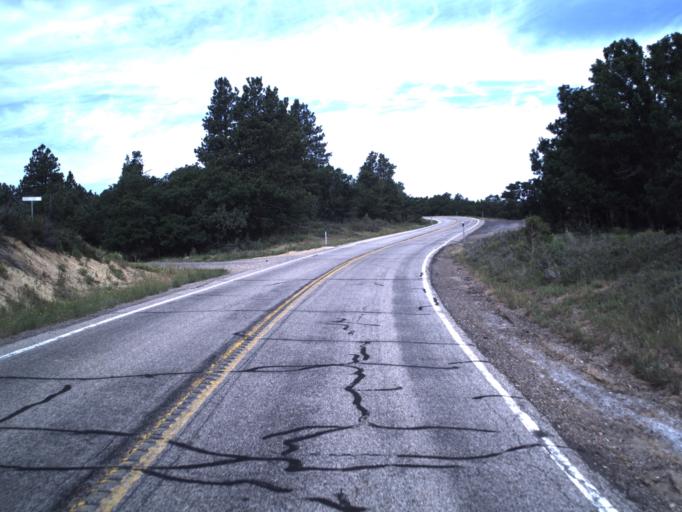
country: US
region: Utah
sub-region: Garfield County
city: Panguitch
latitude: 37.4959
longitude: -112.5416
